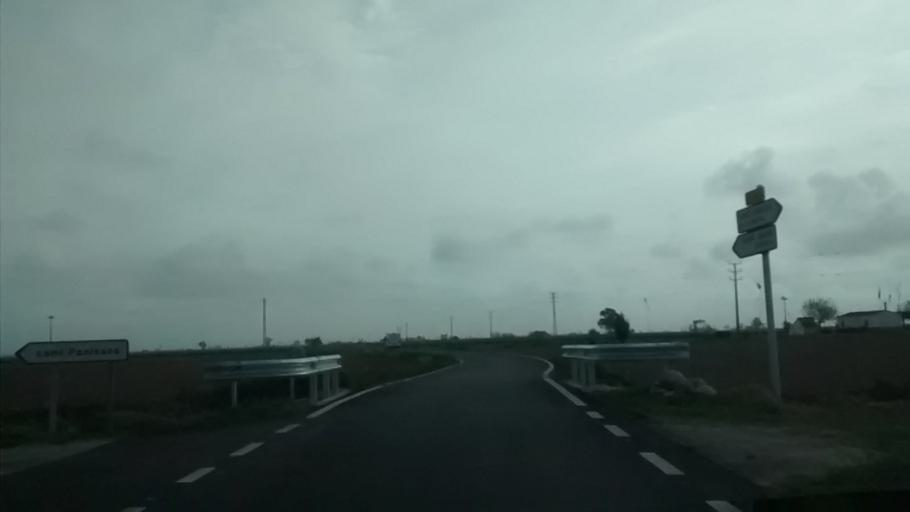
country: ES
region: Catalonia
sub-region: Provincia de Tarragona
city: Sant Carles de la Rapita
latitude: 40.6631
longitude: 0.6425
